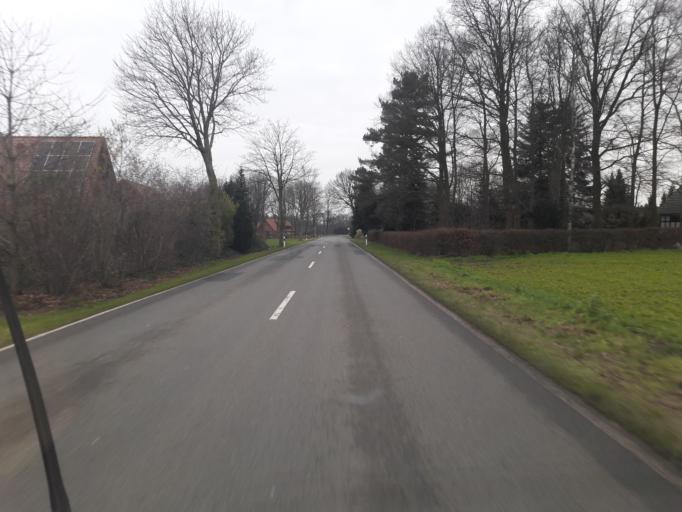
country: DE
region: Lower Saxony
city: Warmsen
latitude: 52.4231
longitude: 8.8557
